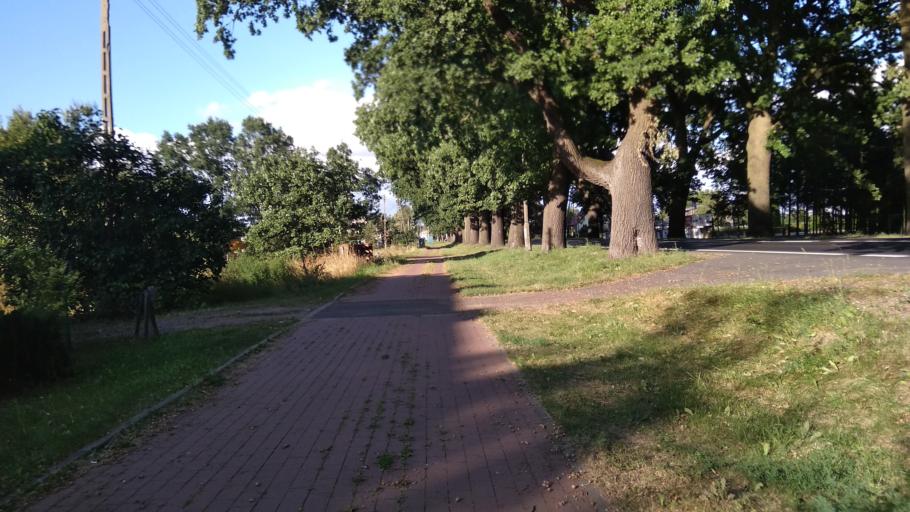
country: PL
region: Kujawsko-Pomorskie
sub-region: Powiat bydgoski
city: Osielsko
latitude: 53.2277
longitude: 18.1338
